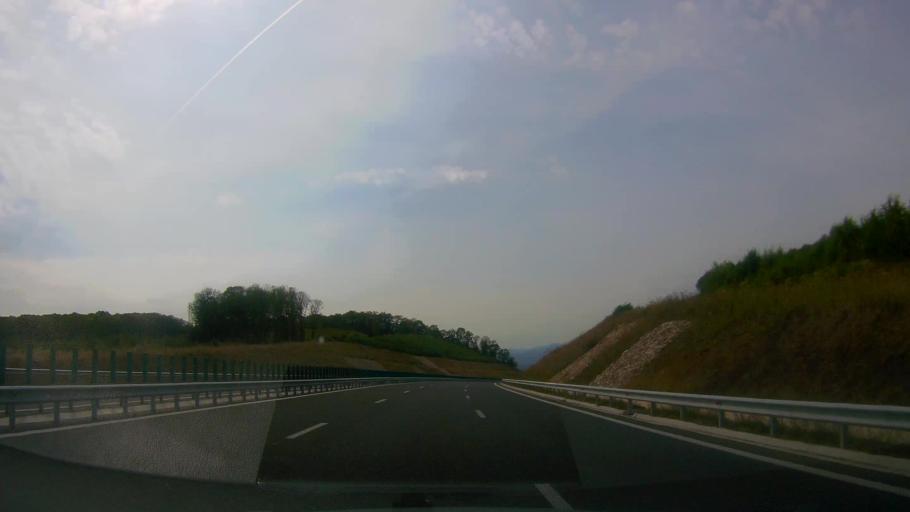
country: RO
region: Cluj
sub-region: Comuna Floresti
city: Luna de Sus
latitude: 46.7839
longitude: 23.4160
